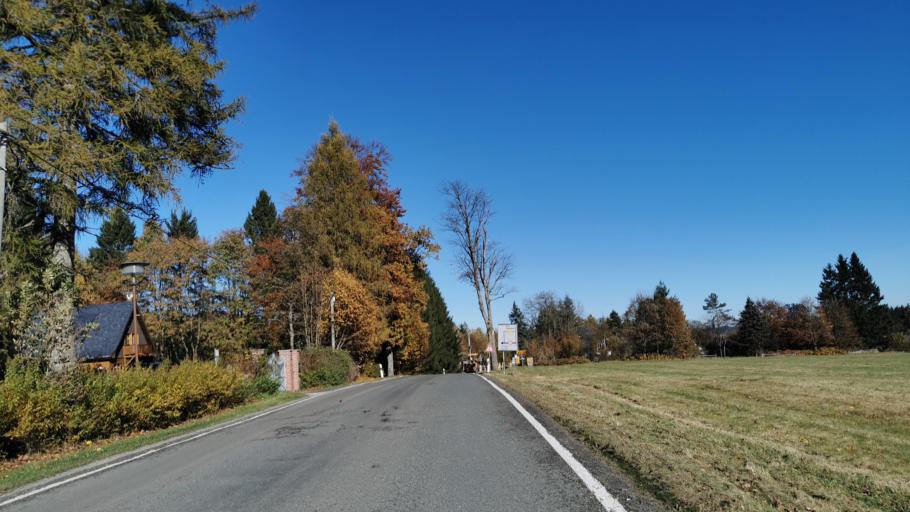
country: DE
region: Thuringia
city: Wurzbach
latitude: 50.4171
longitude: 11.5297
